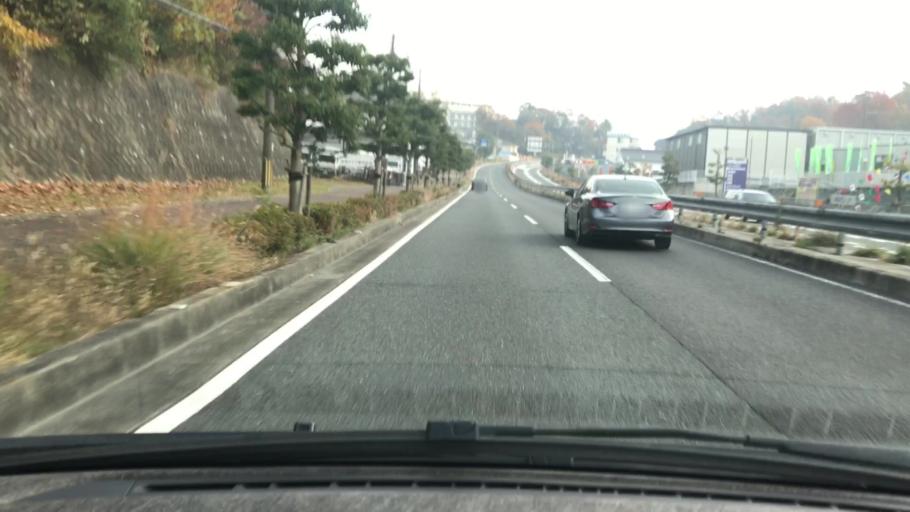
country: JP
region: Hyogo
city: Sandacho
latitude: 34.8293
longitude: 135.2503
